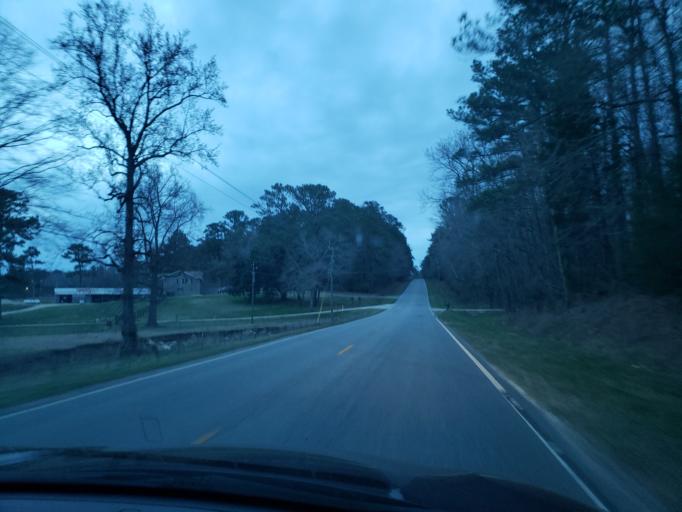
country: US
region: Alabama
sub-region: Lee County
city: Auburn
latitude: 32.6454
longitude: -85.4571
